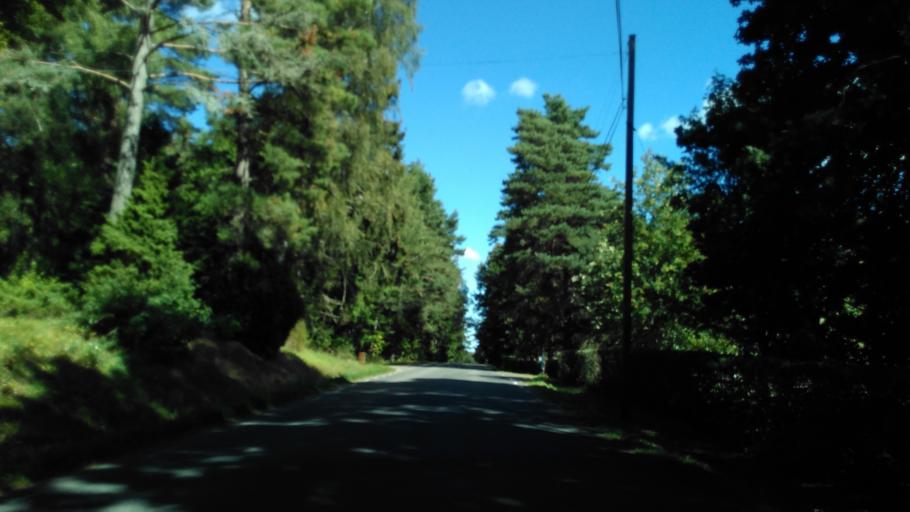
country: SE
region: Vaestra Goetaland
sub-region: Skara Kommun
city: Axvall
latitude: 58.4194
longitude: 13.6135
